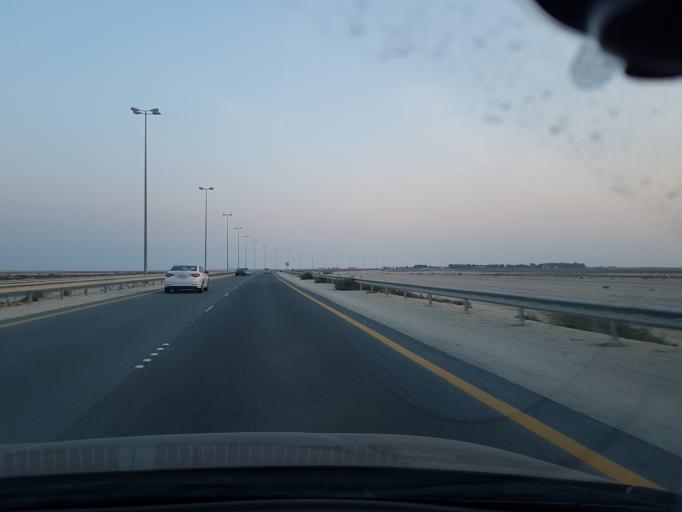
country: BH
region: Central Governorate
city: Dar Kulayb
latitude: 26.0028
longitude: 50.4850
